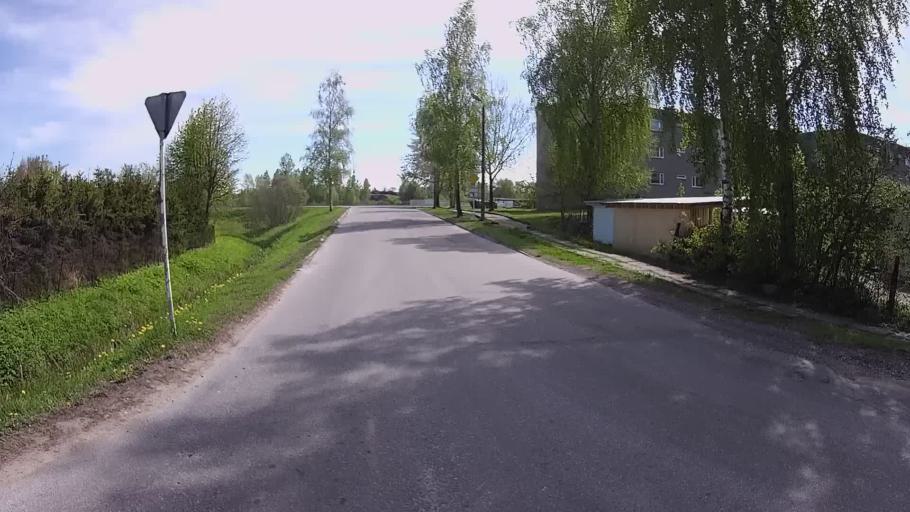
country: EE
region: Valgamaa
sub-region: Valga linn
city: Valga
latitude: 57.7789
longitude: 26.0636
